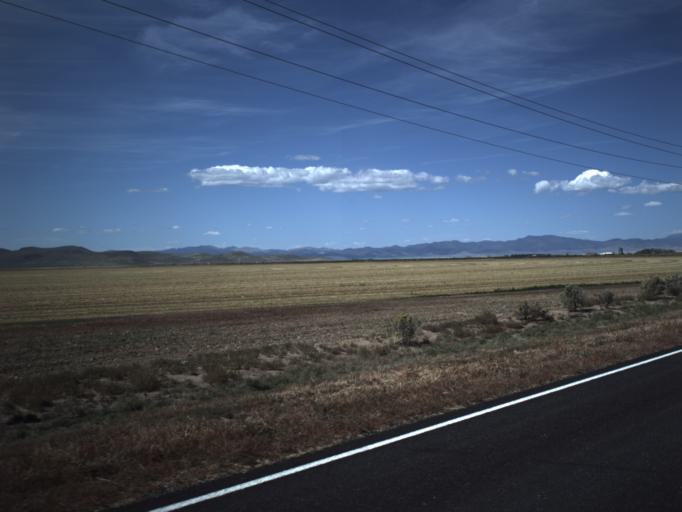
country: US
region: Utah
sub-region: Washington County
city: Enterprise
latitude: 37.6651
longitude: -113.6612
